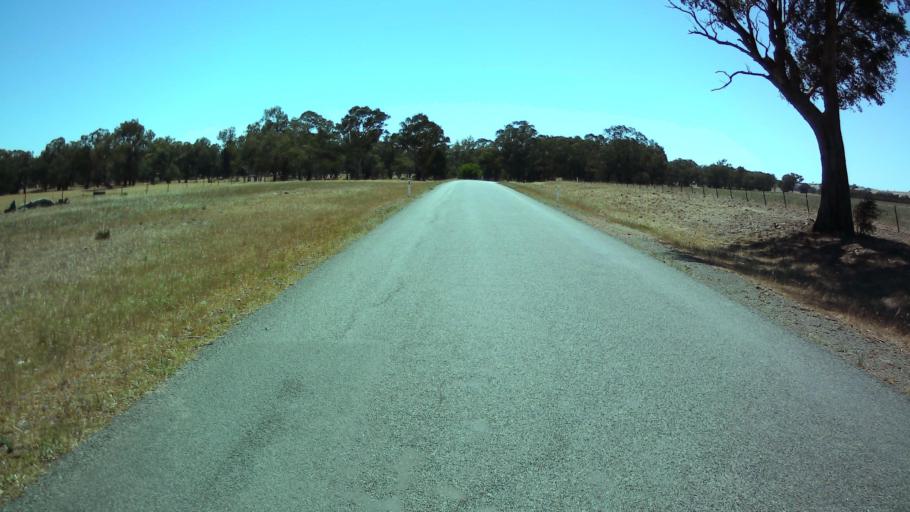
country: AU
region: New South Wales
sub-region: Weddin
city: Grenfell
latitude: -34.0009
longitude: 148.3903
